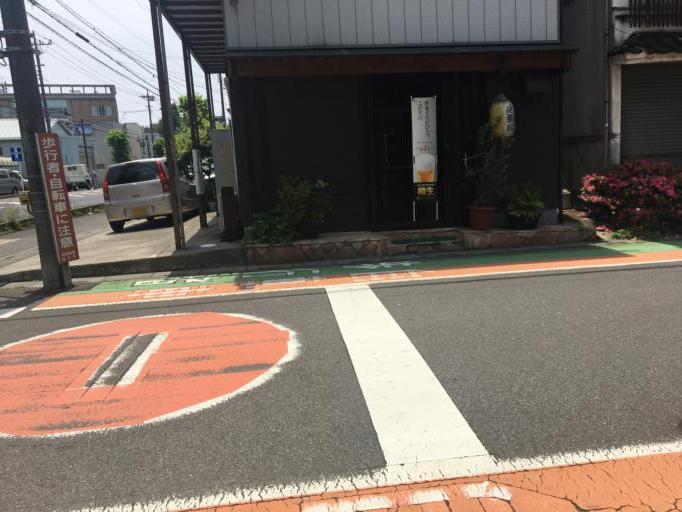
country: JP
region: Saitama
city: Koshigaya
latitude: 35.9009
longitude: 139.7824
